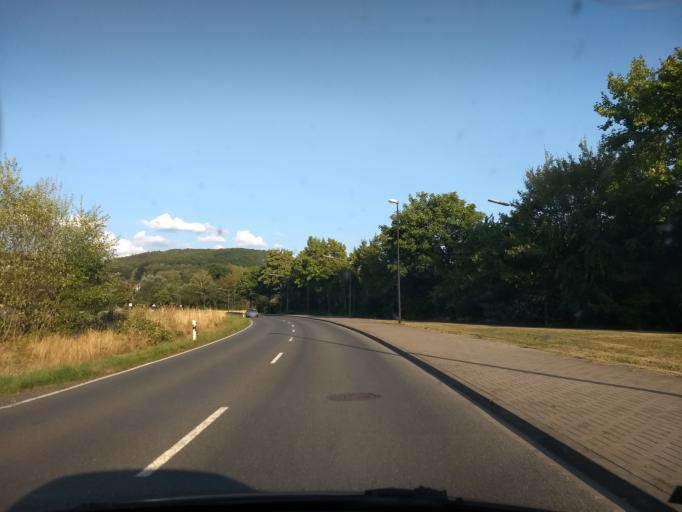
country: DE
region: North Rhine-Westphalia
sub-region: Regierungsbezirk Arnsberg
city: Arnsberg
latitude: 51.3822
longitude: 8.0645
